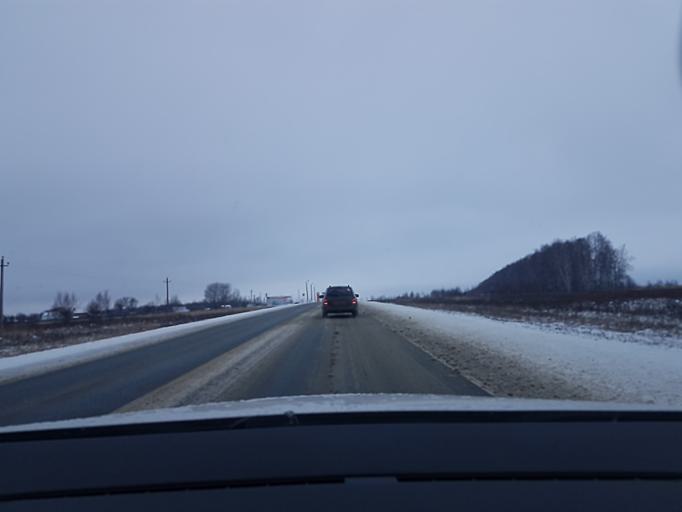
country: RU
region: Moskovskaya
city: Uzunovo
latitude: 54.5795
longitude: 38.4436
